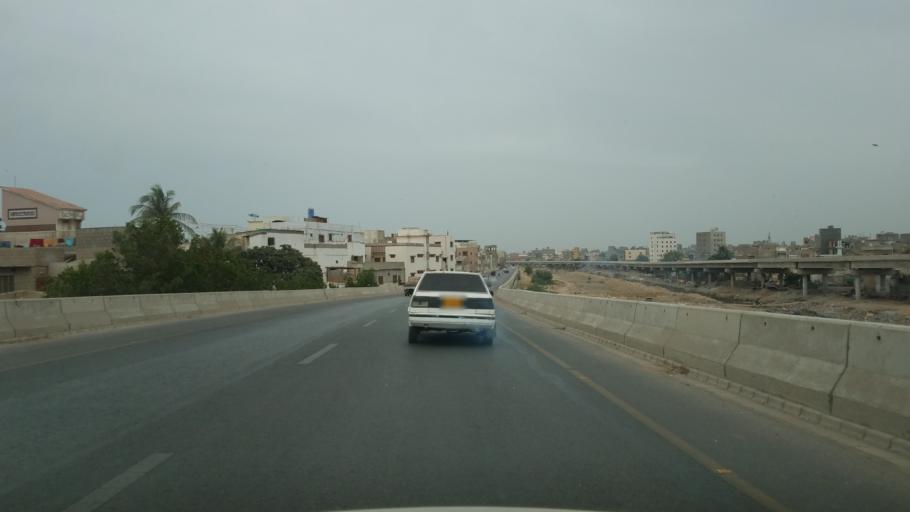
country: PK
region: Sindh
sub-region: Karachi District
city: Karachi
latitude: 24.8984
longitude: 67.0592
